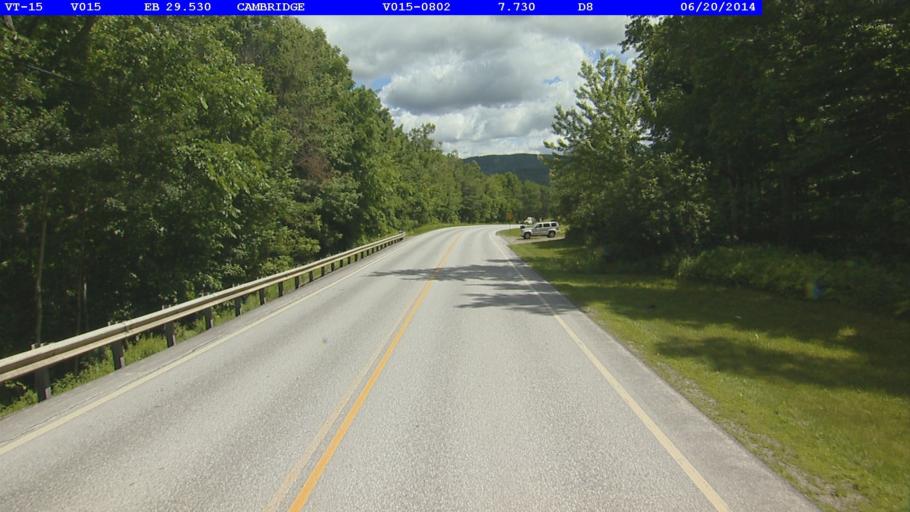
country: US
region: Vermont
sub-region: Lamoille County
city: Johnson
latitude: 44.6654
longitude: -72.7858
